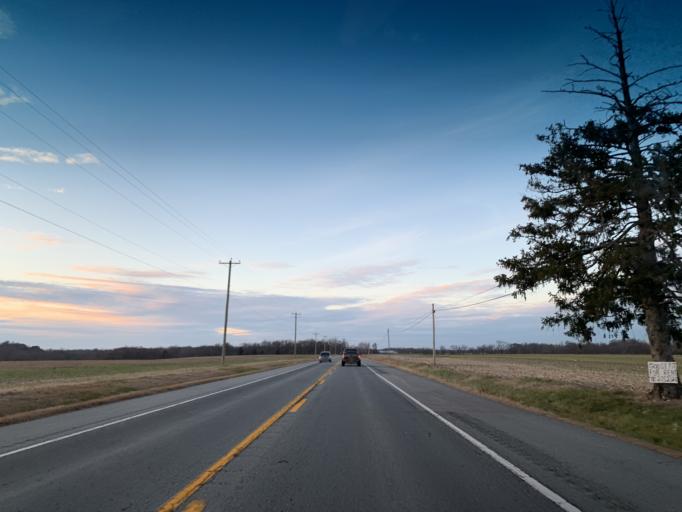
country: US
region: Delaware
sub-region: New Castle County
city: Middletown
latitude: 39.4398
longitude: -75.8630
